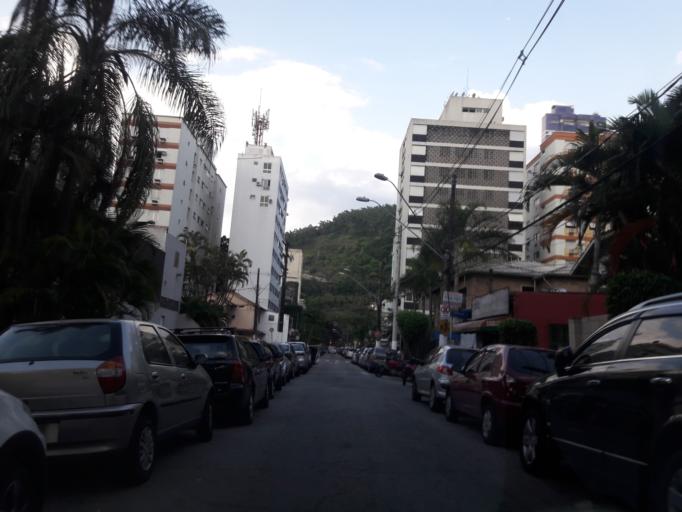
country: BR
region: Sao Paulo
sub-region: Sao Vicente
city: Sao Vicente
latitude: -23.9709
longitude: -46.3703
